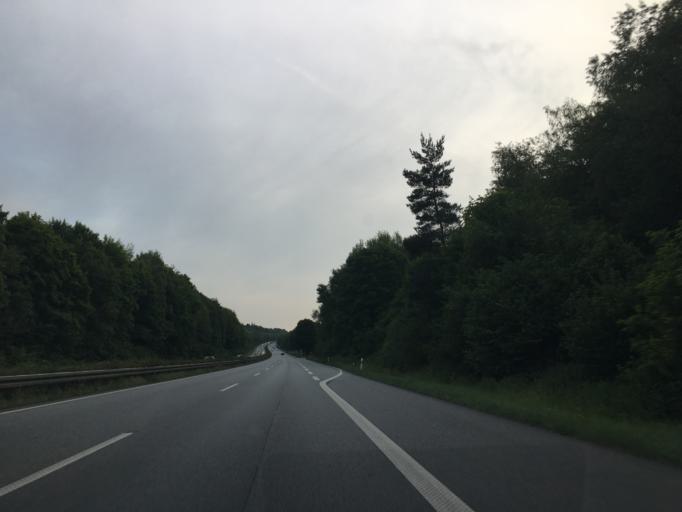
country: DE
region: Hesse
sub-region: Regierungsbezirk Darmstadt
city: Rossdorf
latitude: 49.8693
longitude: 8.7386
